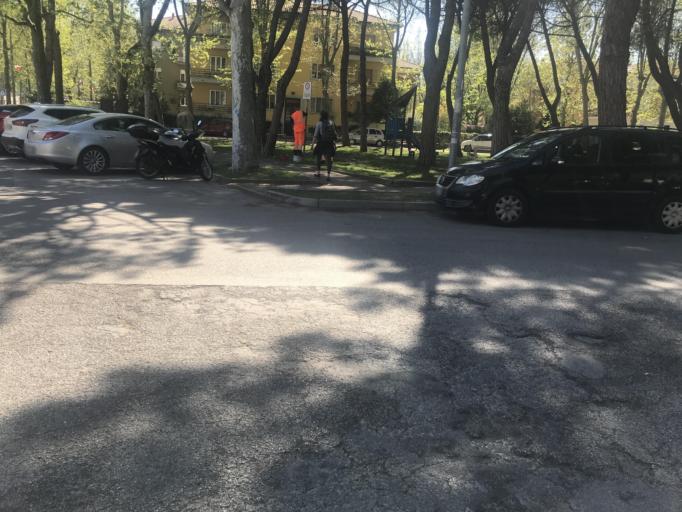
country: IT
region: Emilia-Romagna
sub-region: Provincia di Rimini
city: Rimini
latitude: 44.0537
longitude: 12.5762
